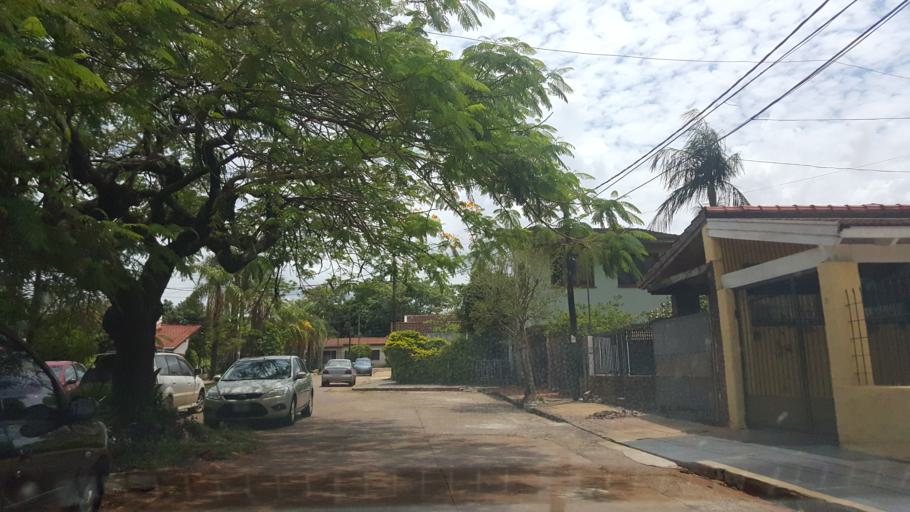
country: AR
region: Misiones
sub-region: Departamento de Capital
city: Posadas
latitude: -27.3807
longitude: -55.9080
